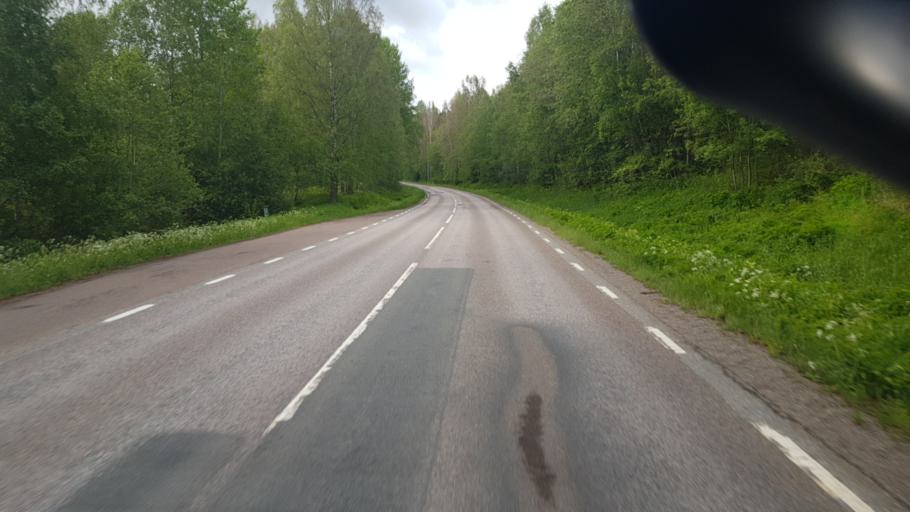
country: SE
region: Vaermland
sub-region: Eda Kommun
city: Amotfors
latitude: 59.6927
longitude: 12.3445
